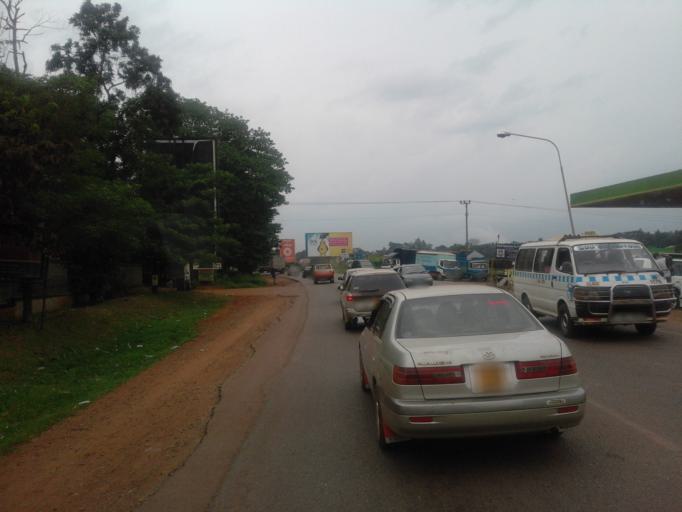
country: UG
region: Eastern Region
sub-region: Jinja District
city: Jinja
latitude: 0.4442
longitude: 33.1933
